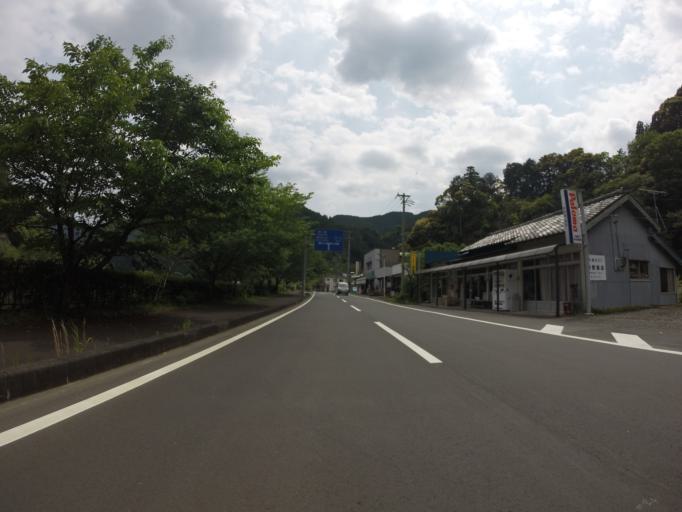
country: JP
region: Shizuoka
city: Shizuoka-shi
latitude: 35.1127
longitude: 138.3267
